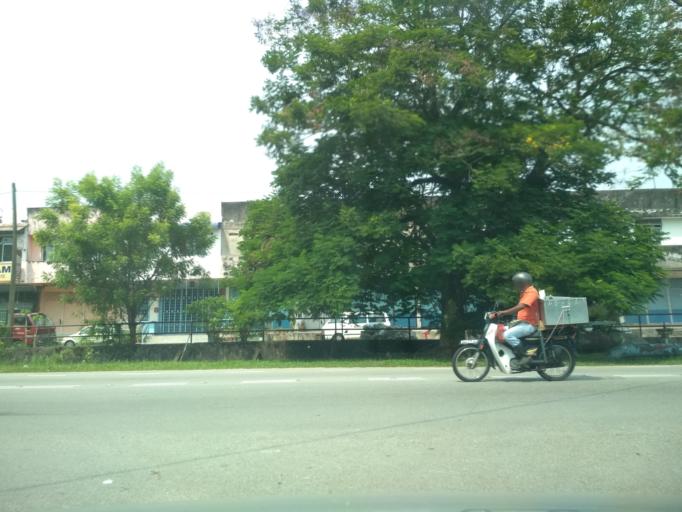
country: MY
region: Kedah
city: Kulim
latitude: 5.3752
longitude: 100.5666
